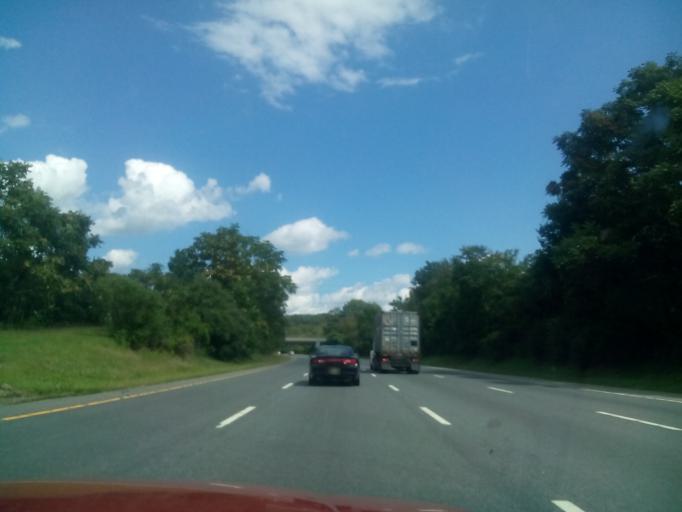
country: US
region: New Jersey
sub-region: Warren County
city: Belvidere
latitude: 40.9224
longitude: -75.0618
